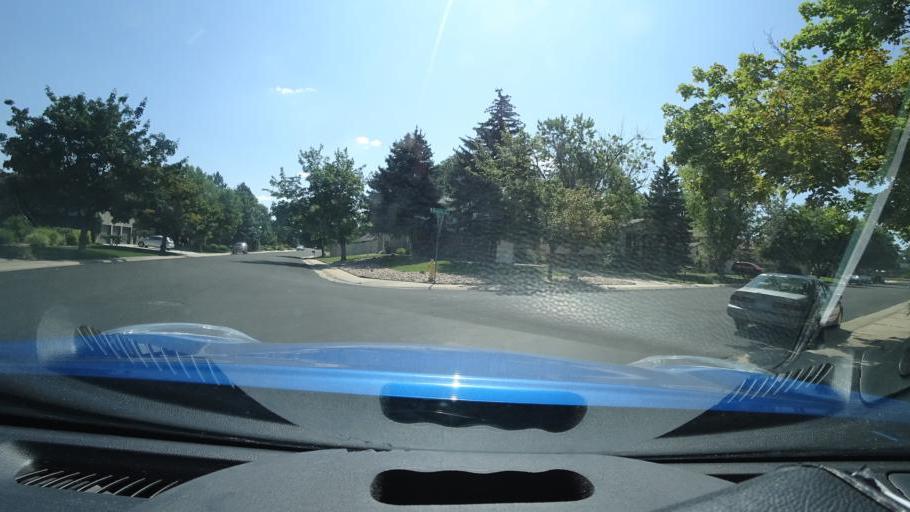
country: US
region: Colorado
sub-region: Adams County
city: Aurora
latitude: 39.7126
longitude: -104.8388
